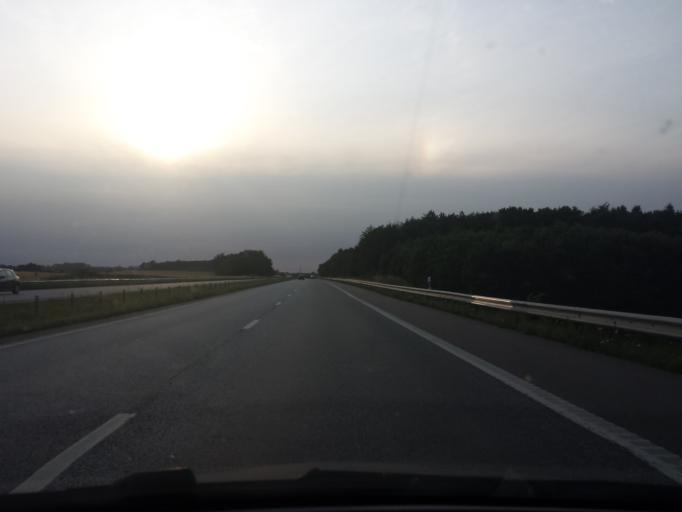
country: SE
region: Skane
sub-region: Malmo
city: Oxie
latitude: 55.5450
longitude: 13.1478
